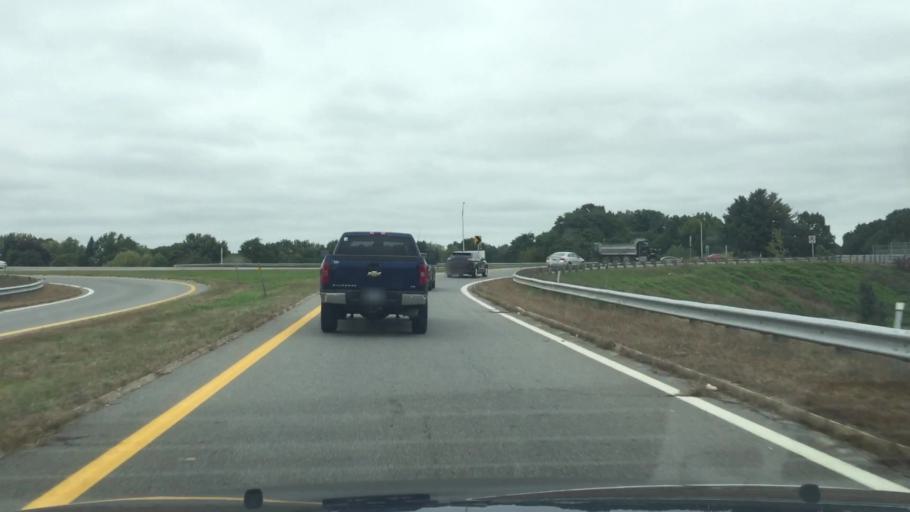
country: US
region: New Hampshire
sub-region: Hillsborough County
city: Hudson
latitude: 42.7227
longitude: -71.4400
